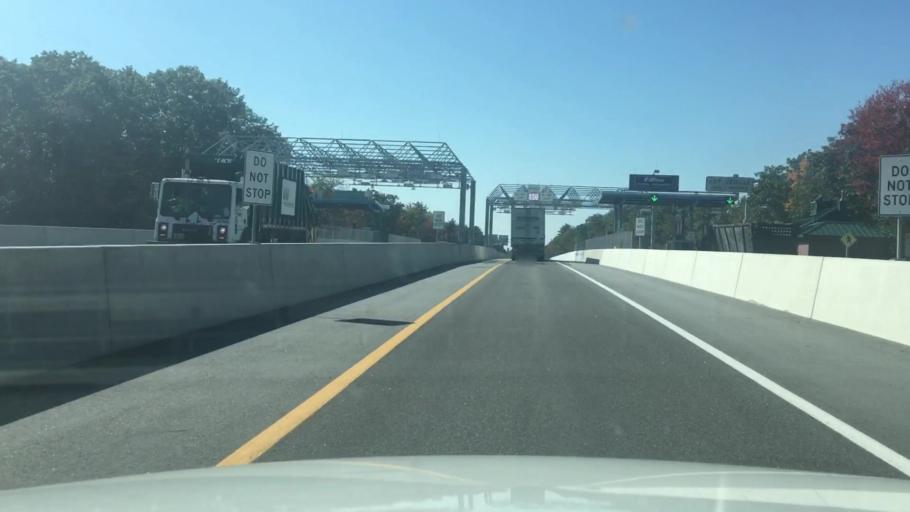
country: US
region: Maine
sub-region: Cumberland County
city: Falmouth
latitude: 43.7335
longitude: -70.2536
